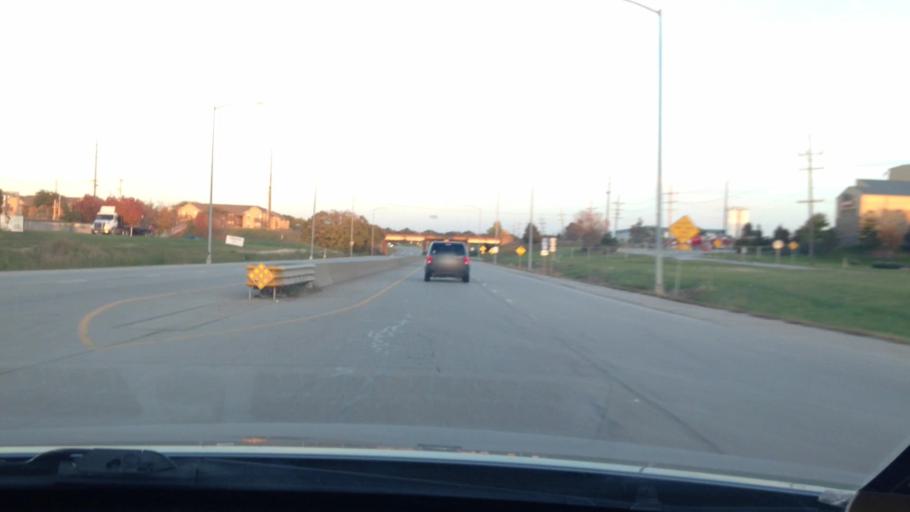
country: US
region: Kansas
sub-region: Johnson County
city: Olathe
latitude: 38.8677
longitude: -94.8098
